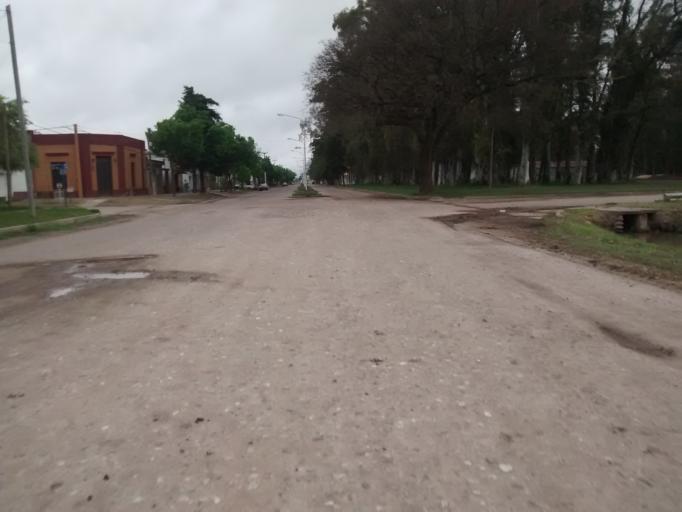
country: AR
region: Santa Fe
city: Galvez
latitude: -31.9022
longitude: -61.2814
